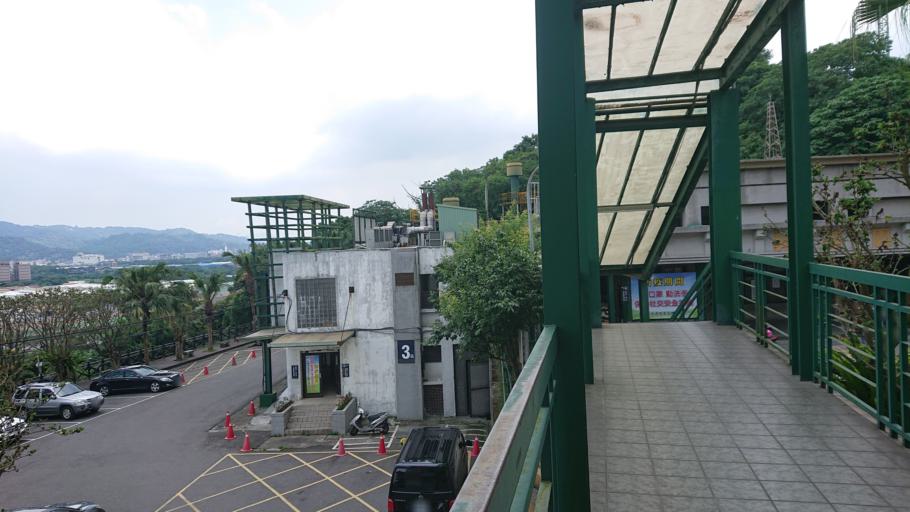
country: TW
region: Taipei
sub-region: Taipei
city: Banqiao
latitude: 24.9483
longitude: 121.4080
